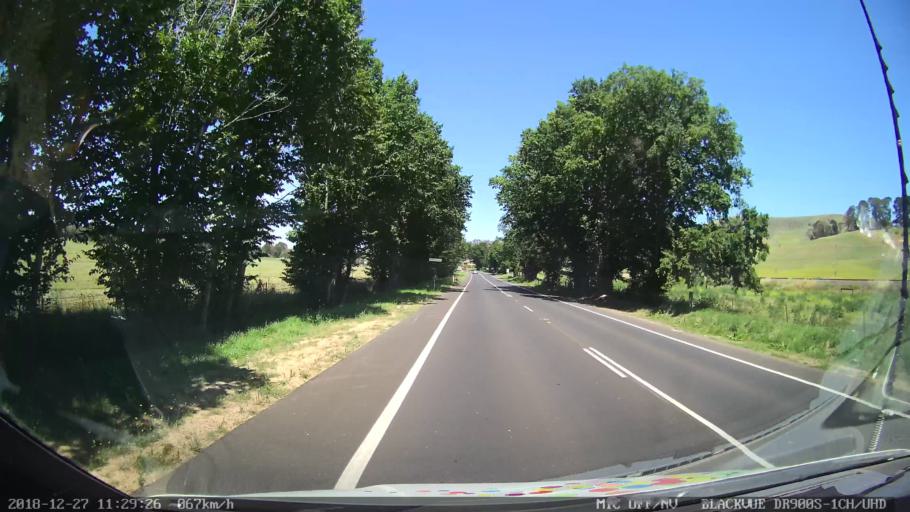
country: AU
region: New South Wales
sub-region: Bathurst Regional
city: Perthville
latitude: -33.4828
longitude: 149.5523
